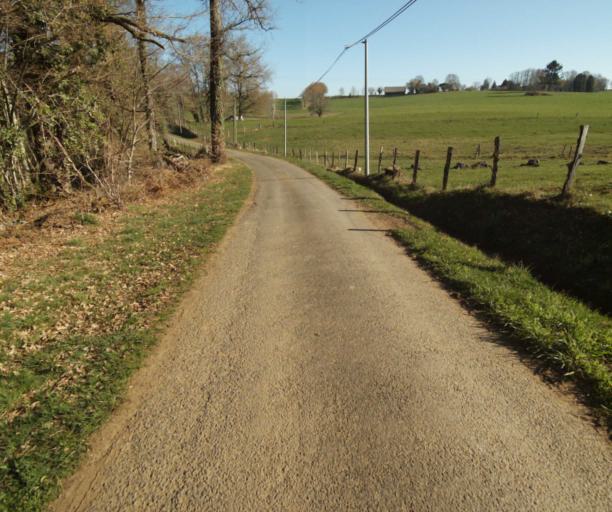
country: FR
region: Limousin
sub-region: Departement de la Correze
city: Saint-Clement
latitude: 45.3789
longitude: 1.6543
